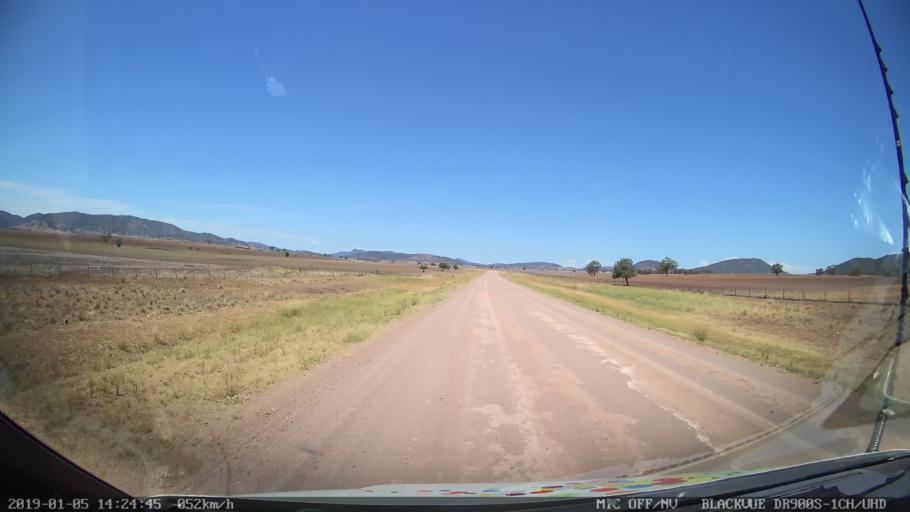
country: AU
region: New South Wales
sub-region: Liverpool Plains
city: Quirindi
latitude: -31.2411
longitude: 150.5429
